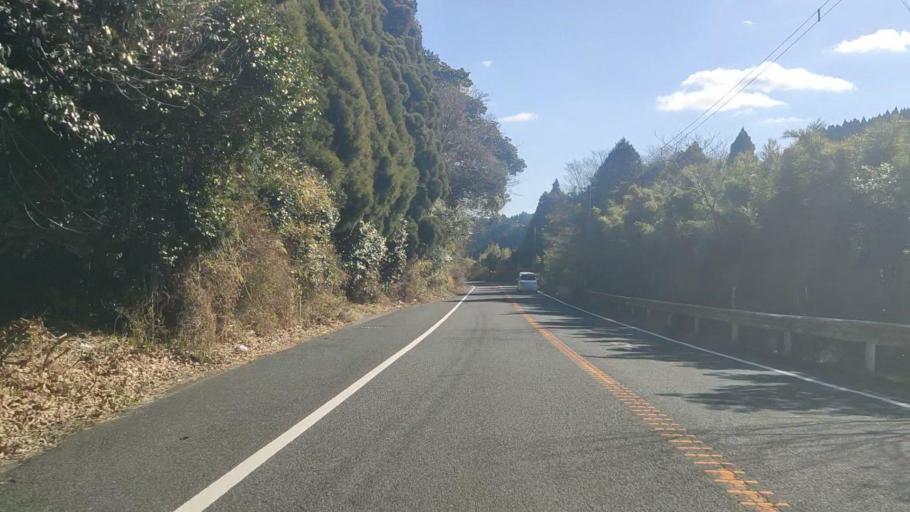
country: JP
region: Kagoshima
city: Sueyoshicho-ninokata
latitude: 31.6620
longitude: 130.8886
